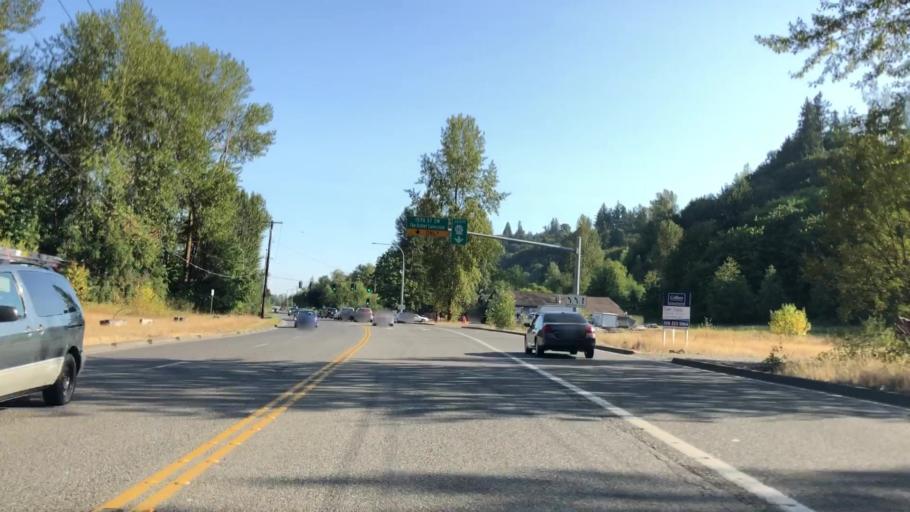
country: US
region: Washington
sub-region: King County
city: Algona
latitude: 47.2970
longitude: -122.2605
